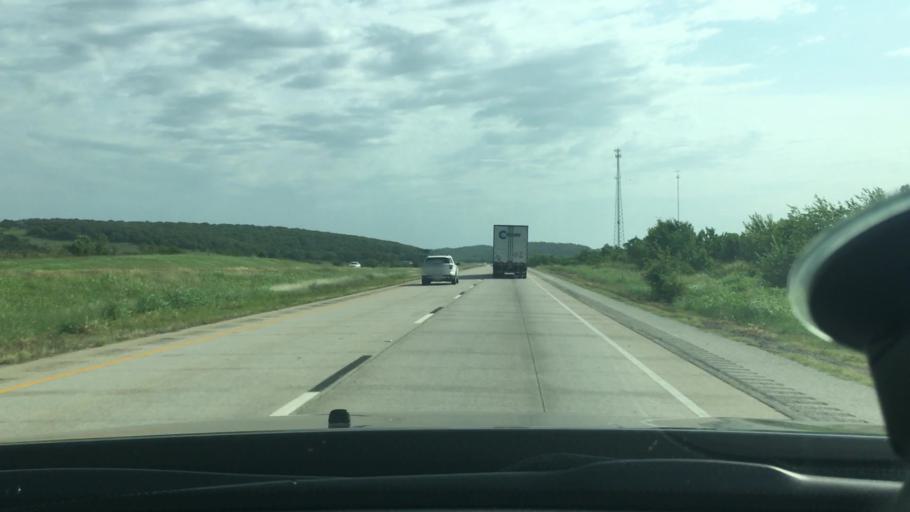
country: US
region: Oklahoma
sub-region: Atoka County
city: Atoka
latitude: 34.4262
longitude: -96.0888
